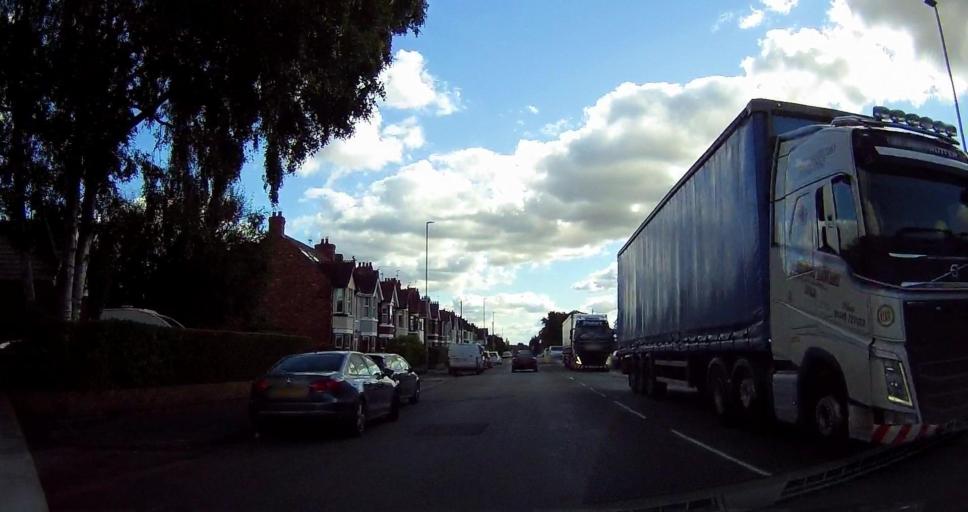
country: GB
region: England
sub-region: Staffordshire
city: Stafford
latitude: 52.8270
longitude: -2.1291
